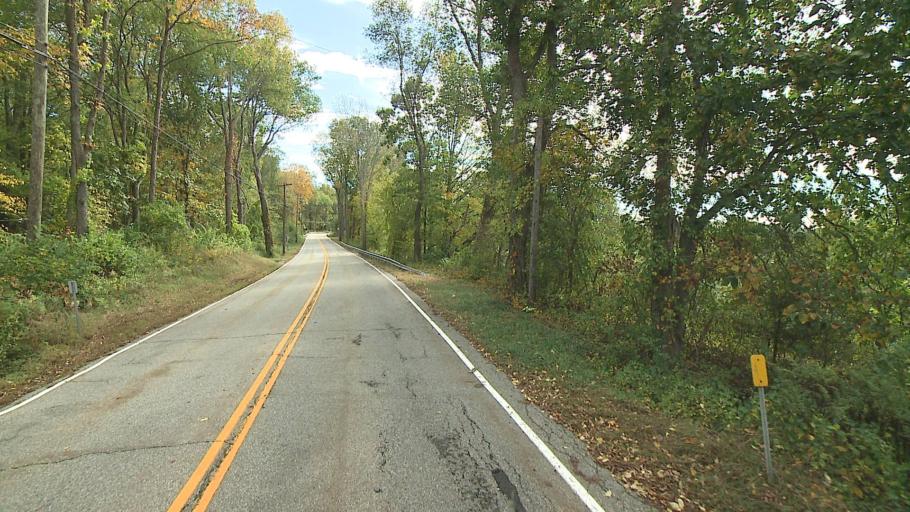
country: US
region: Connecticut
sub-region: Windham County
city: Putnam
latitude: 41.8897
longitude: -71.8774
